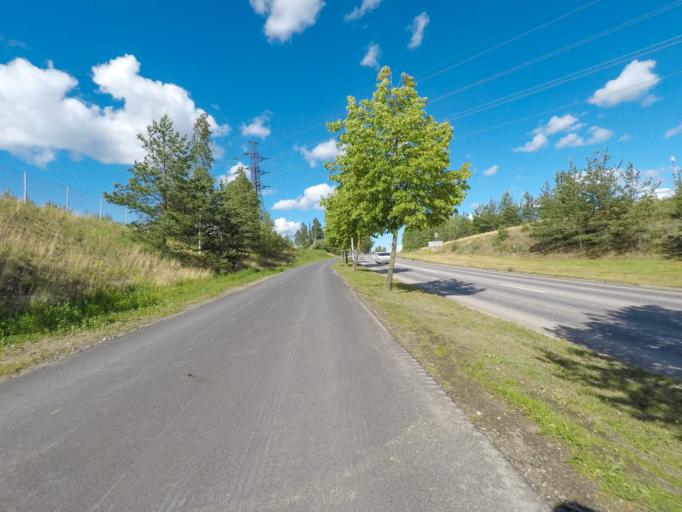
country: FI
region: South Karelia
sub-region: Lappeenranta
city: Lappeenranta
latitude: 61.0639
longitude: 28.2545
